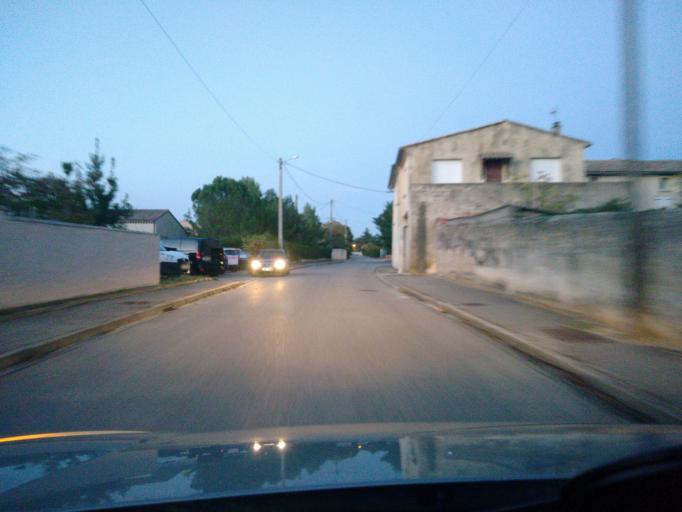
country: FR
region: Rhone-Alpes
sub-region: Departement de la Drome
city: Montelimar
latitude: 44.5402
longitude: 4.7550
